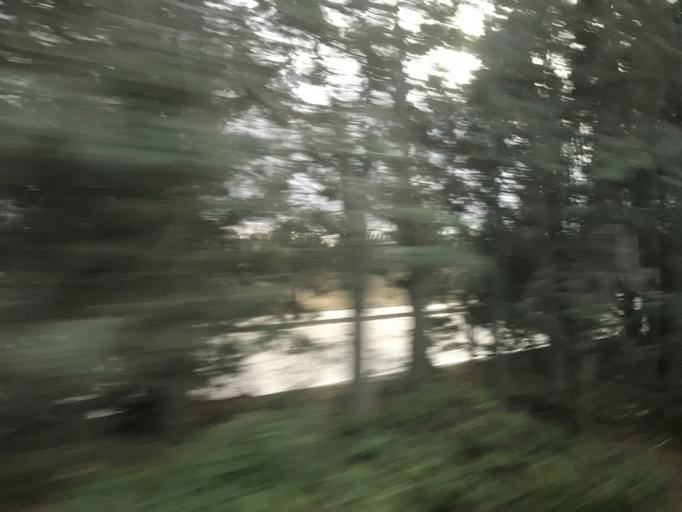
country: ES
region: Castille and Leon
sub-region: Provincia de Valladolid
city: Valladolid
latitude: 41.6476
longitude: -4.7544
